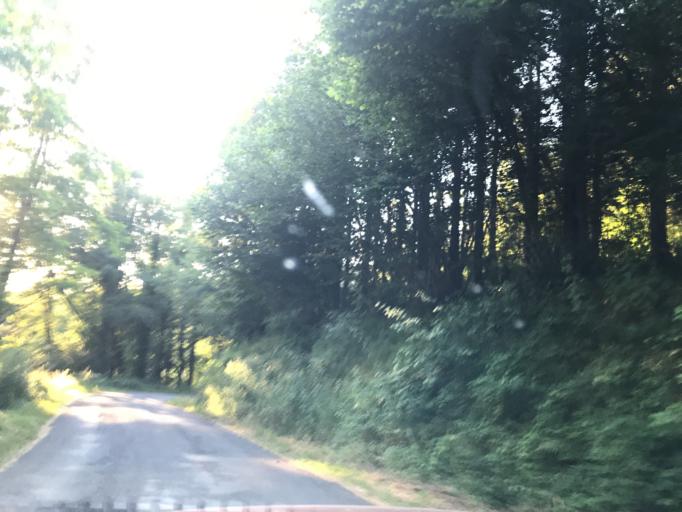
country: FR
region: Auvergne
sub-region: Departement du Puy-de-Dome
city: Courpiere
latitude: 45.7532
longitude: 3.6202
